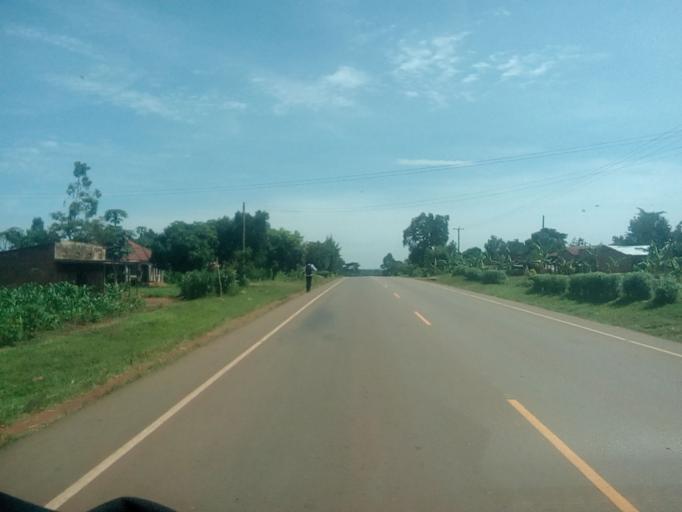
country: UG
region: Eastern Region
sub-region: Jinja District
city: Buwenge
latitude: 0.6368
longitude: 33.1782
